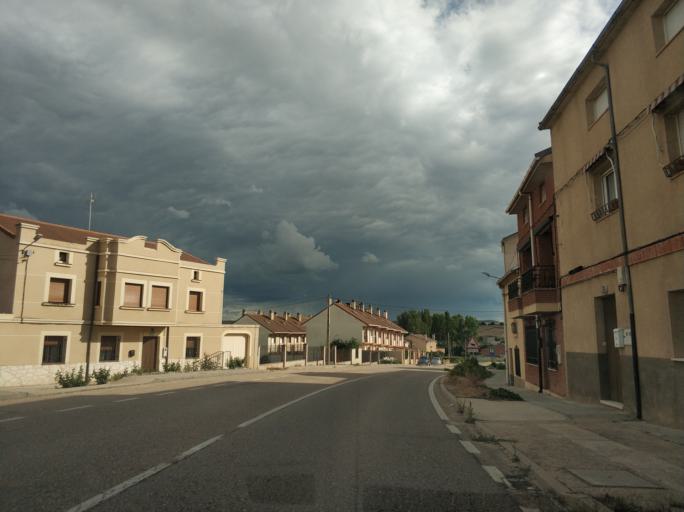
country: ES
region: Castille and Leon
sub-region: Provincia de Burgos
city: Castrillo de la Vega
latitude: 41.6511
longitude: -3.7790
